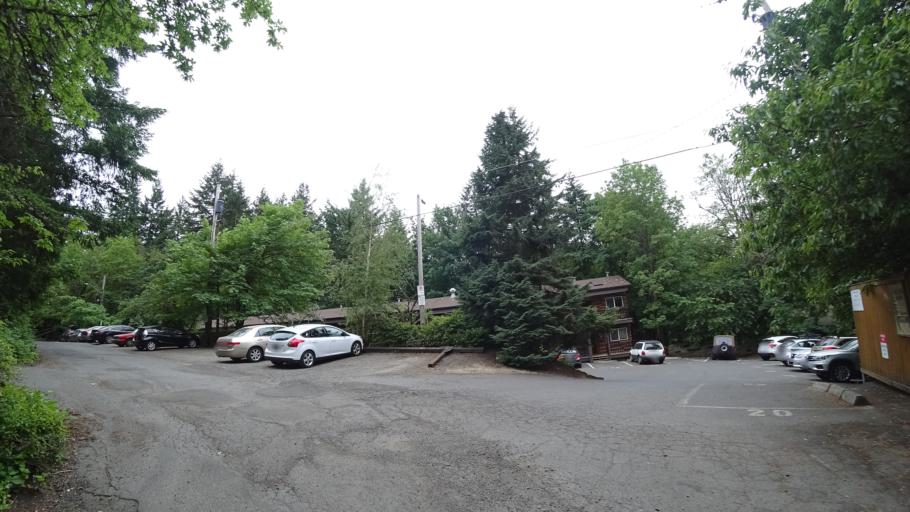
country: US
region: Oregon
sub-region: Multnomah County
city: Portland
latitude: 45.5005
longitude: -122.6932
